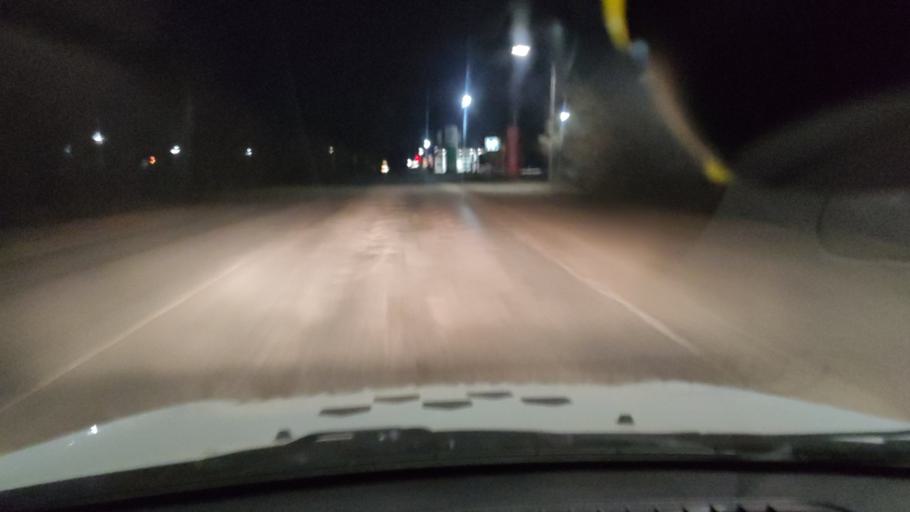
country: RU
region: Samara
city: Podstepki
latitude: 53.5707
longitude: 49.0878
